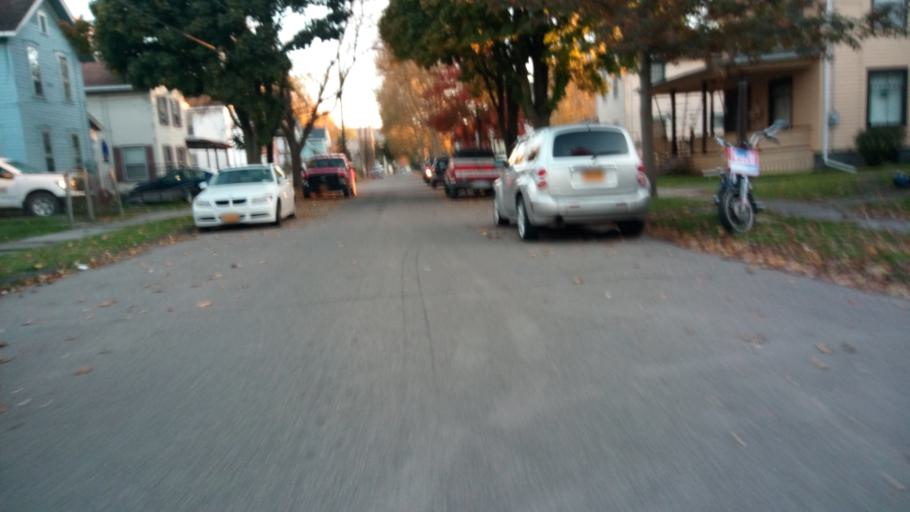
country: US
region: New York
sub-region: Chemung County
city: Elmira
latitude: 42.0754
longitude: -76.8082
